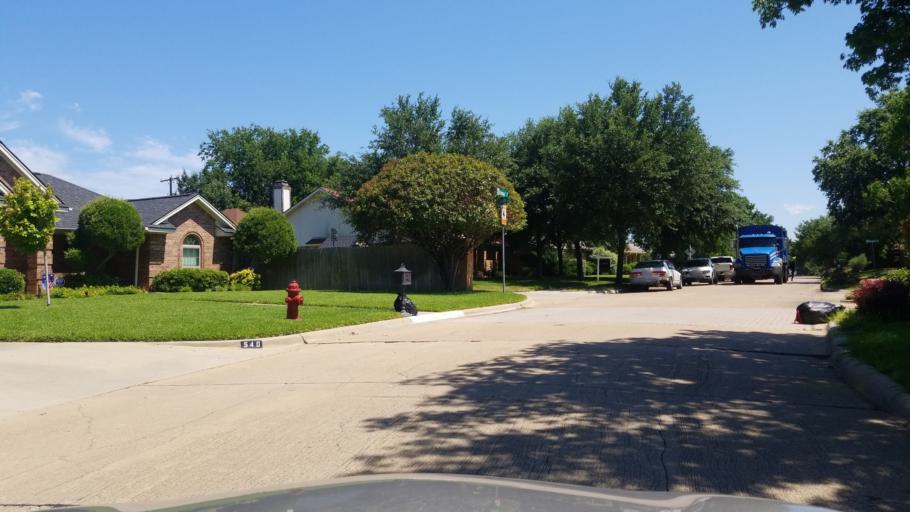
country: US
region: Texas
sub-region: Dallas County
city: Grand Prairie
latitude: 32.6870
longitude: -96.9988
